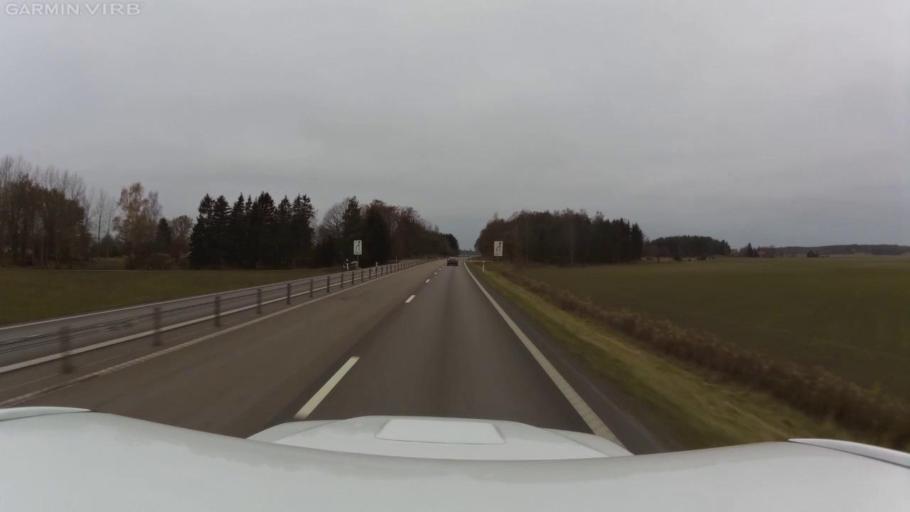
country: SE
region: OEstergoetland
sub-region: Linkopings Kommun
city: Malmslatt
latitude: 58.3746
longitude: 15.4846
